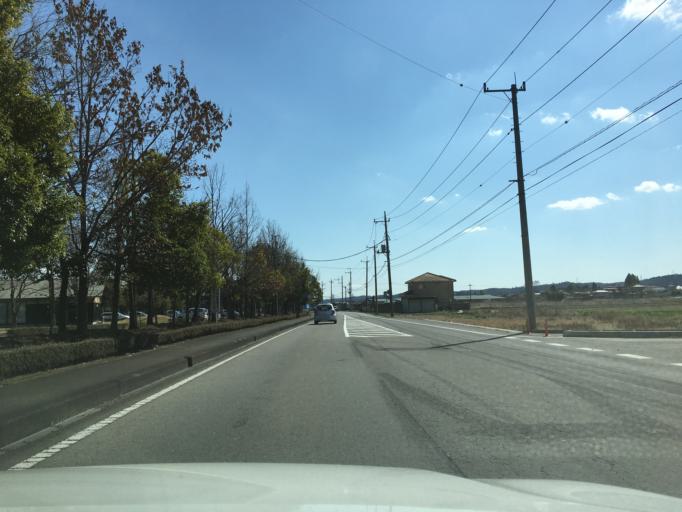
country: JP
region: Tochigi
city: Karasuyama
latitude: 36.7668
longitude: 140.1349
